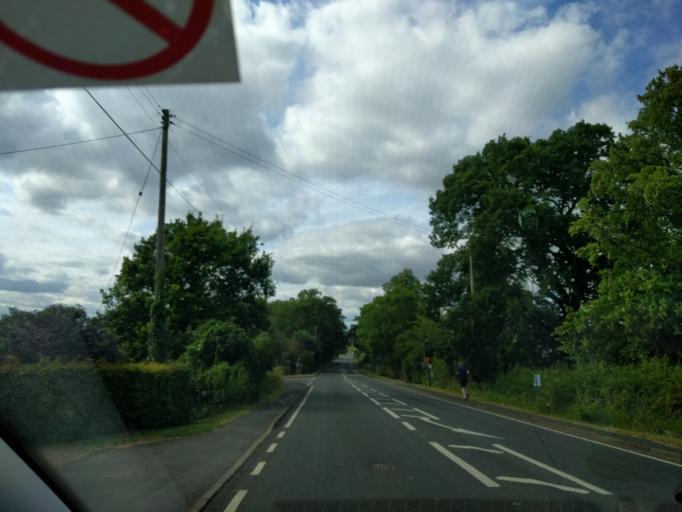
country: GB
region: England
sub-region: Warwickshire
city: Shipston on Stour
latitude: 52.1175
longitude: -1.6428
